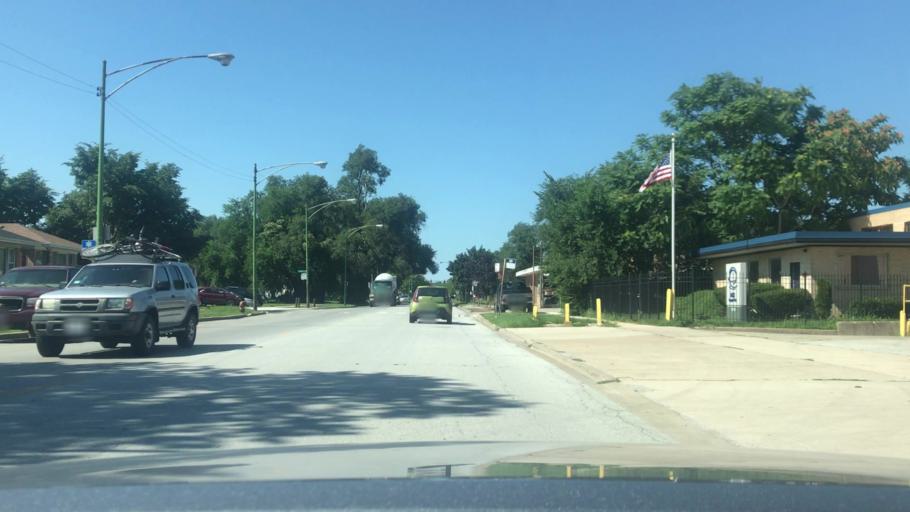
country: US
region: Indiana
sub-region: Lake County
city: Whiting
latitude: 41.7113
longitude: -87.5597
